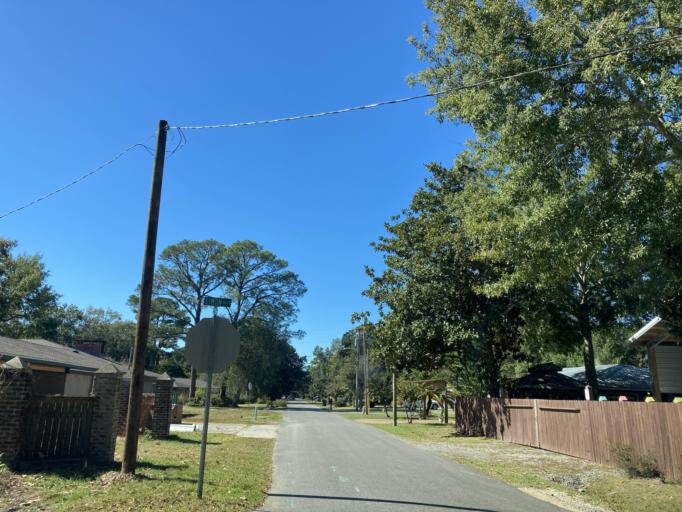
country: US
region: Mississippi
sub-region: Jackson County
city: Ocean Springs
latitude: 30.4092
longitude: -88.8121
